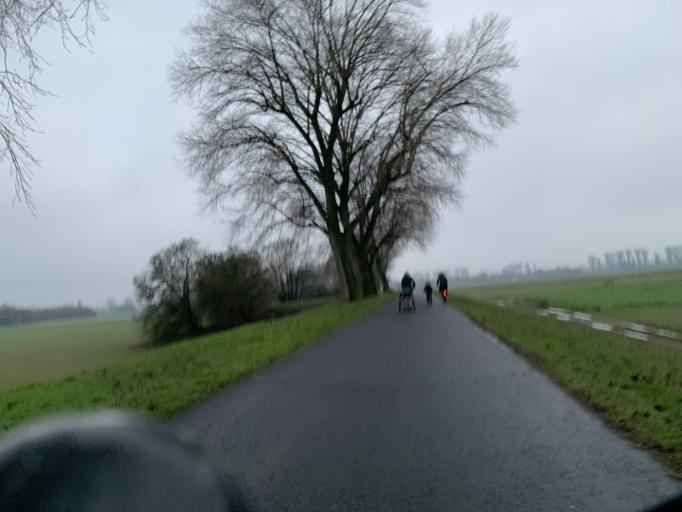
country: DE
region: North Rhine-Westphalia
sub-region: Regierungsbezirk Dusseldorf
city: Meerbusch
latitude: 51.2731
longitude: 6.7119
